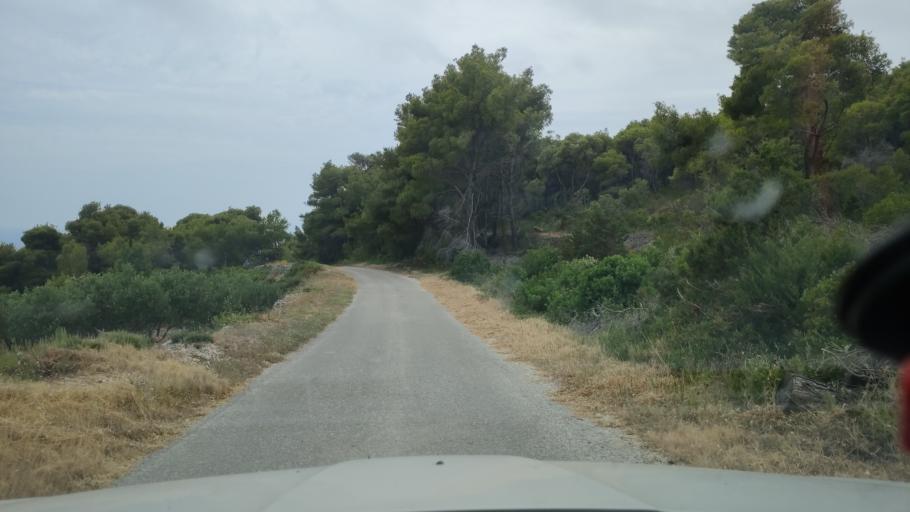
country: HR
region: Splitsko-Dalmatinska
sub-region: Grad Vis
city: Vis
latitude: 43.0275
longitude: 16.1679
